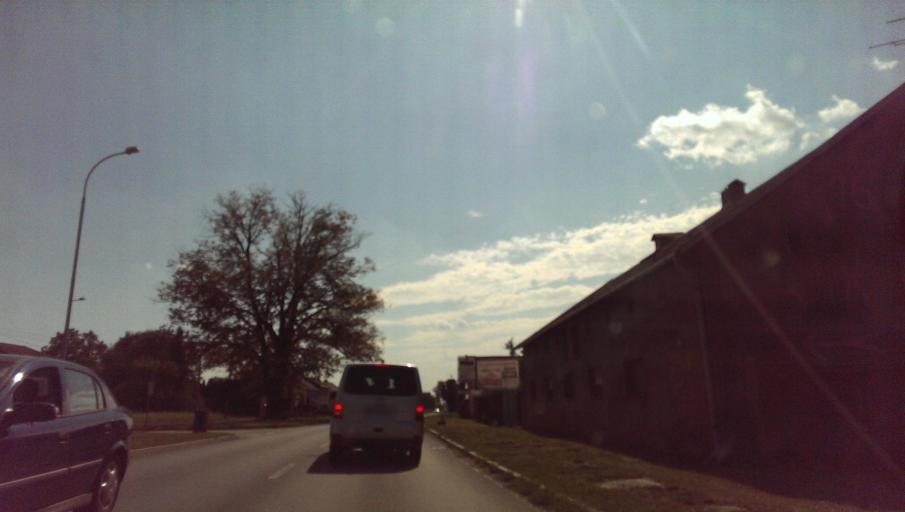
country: CZ
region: Zlin
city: Holesov
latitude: 49.3422
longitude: 17.6023
